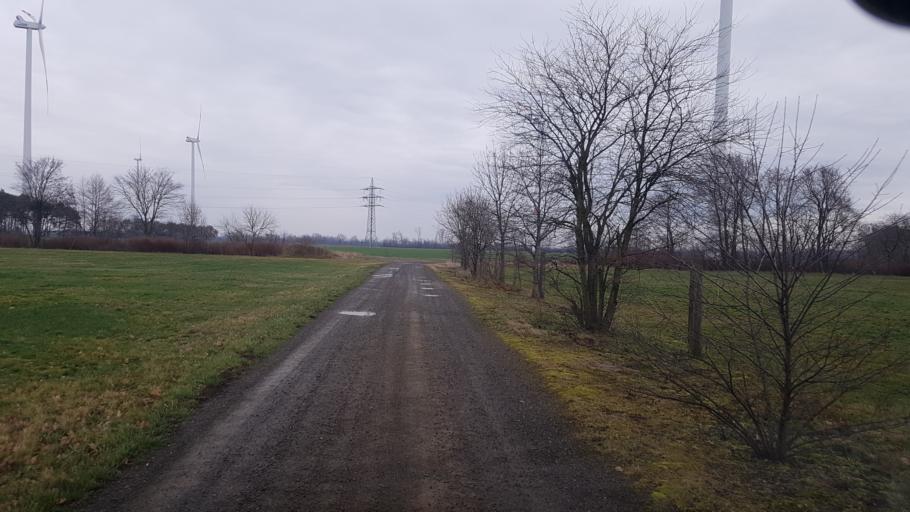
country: DE
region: Brandenburg
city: Bad Liebenwerda
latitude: 51.5211
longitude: 13.3223
